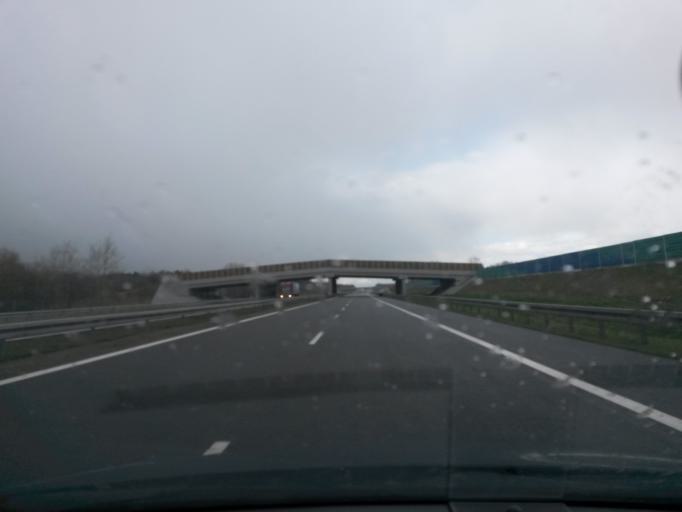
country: PL
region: Greater Poland Voivodeship
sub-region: Powiat koninski
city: Stare Miasto
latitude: 52.1721
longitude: 18.1563
